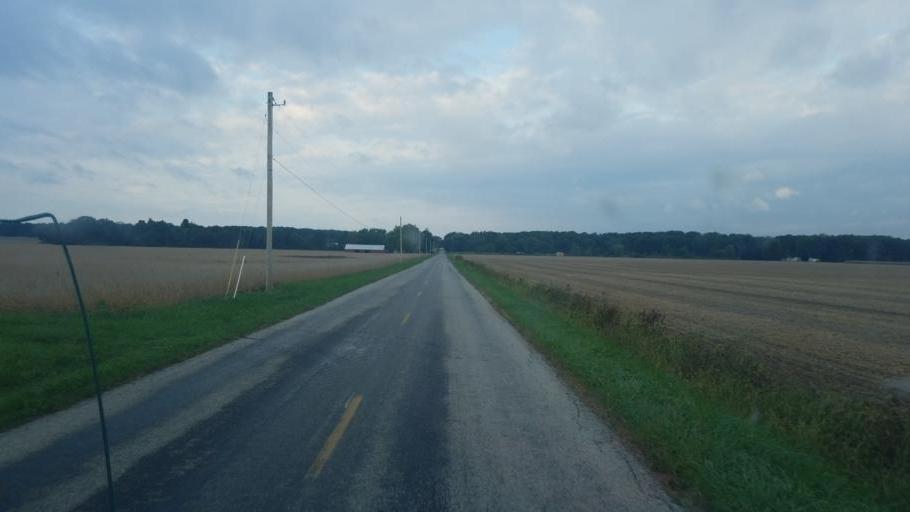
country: US
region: Ohio
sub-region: Marion County
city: Marion
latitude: 40.6736
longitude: -83.1503
